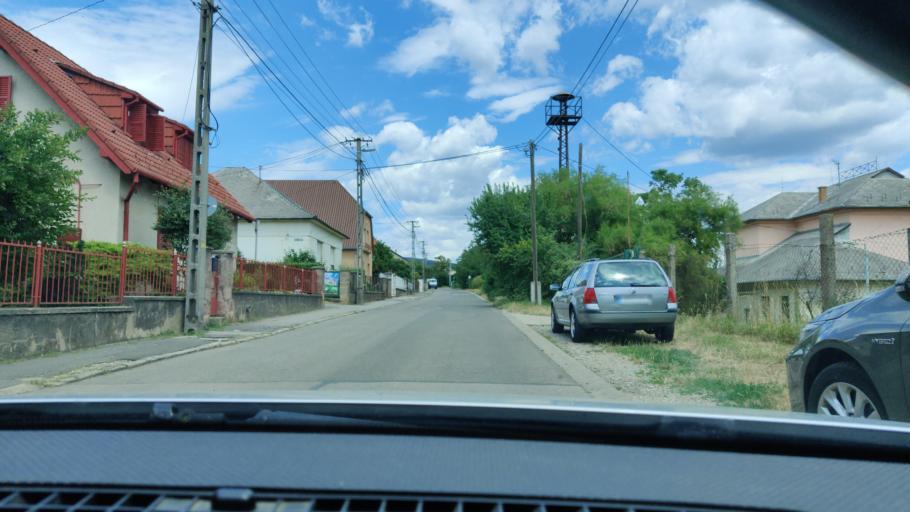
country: HU
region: Baranya
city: Pecs
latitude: 46.0881
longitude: 18.2613
